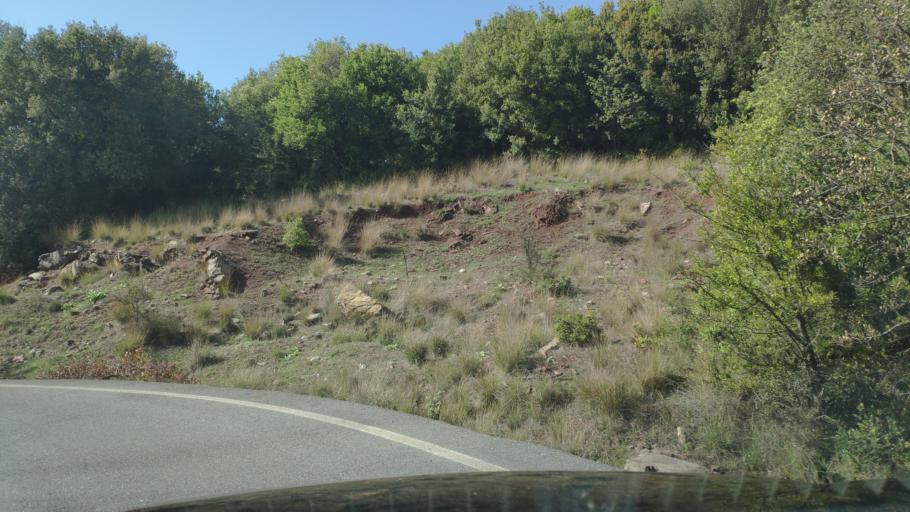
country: GR
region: Peloponnese
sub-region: Nomos Arkadias
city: Dimitsana
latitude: 37.5615
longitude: 21.9983
